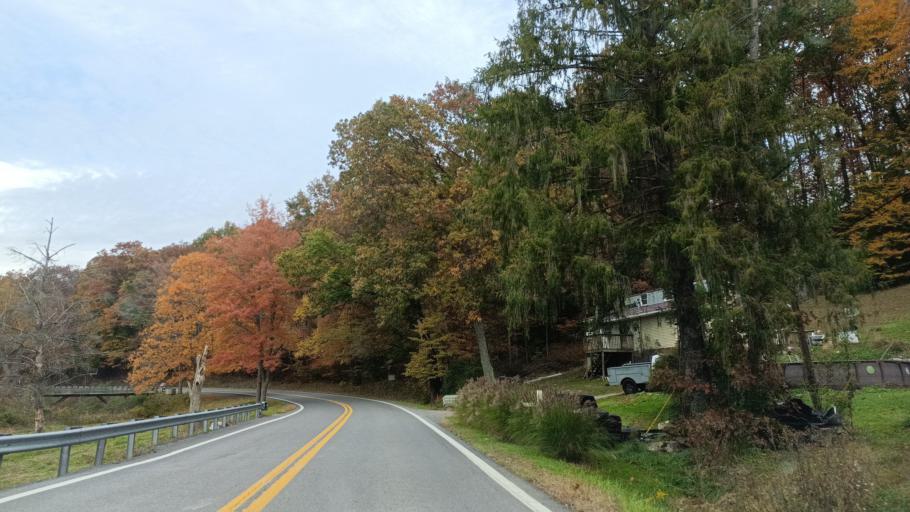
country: US
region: West Virginia
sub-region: Taylor County
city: Grafton
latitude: 39.3346
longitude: -79.8989
